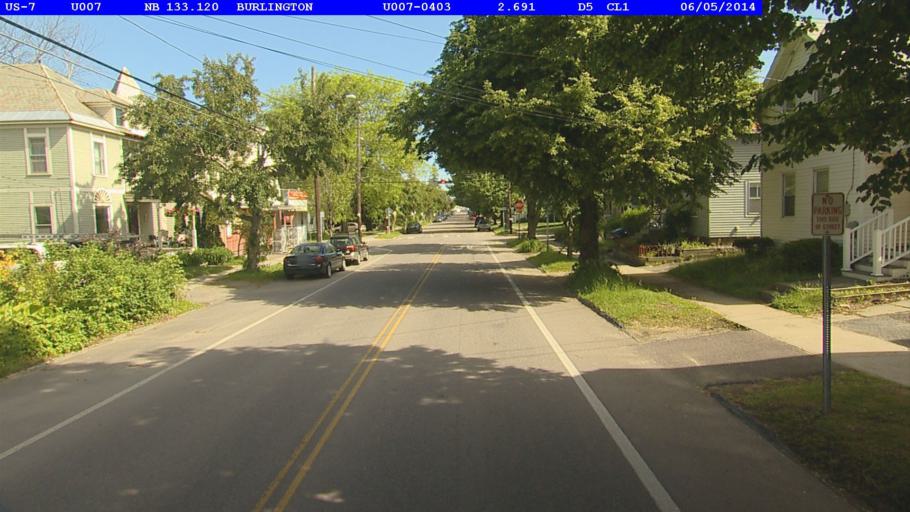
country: US
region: Vermont
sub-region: Chittenden County
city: Burlington
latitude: 44.4845
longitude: -73.2058
